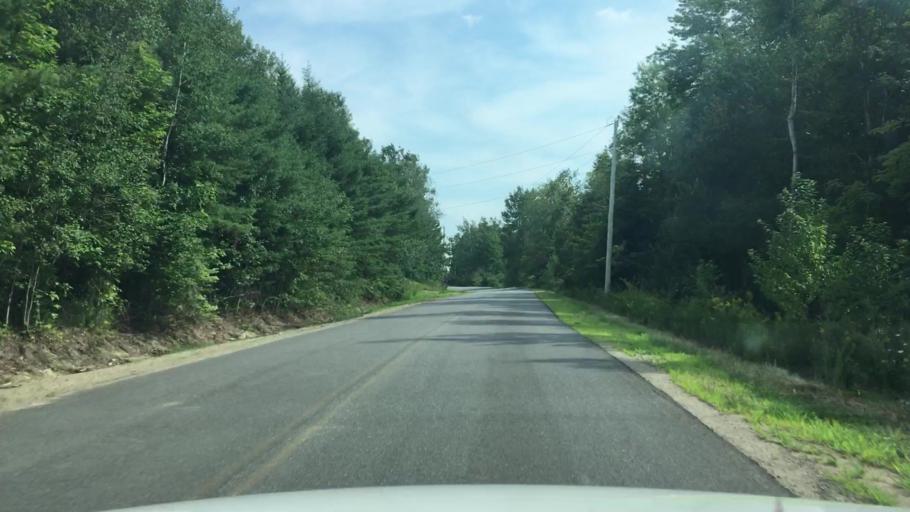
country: US
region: Maine
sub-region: Lincoln County
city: Jefferson
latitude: 44.2418
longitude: -69.4454
